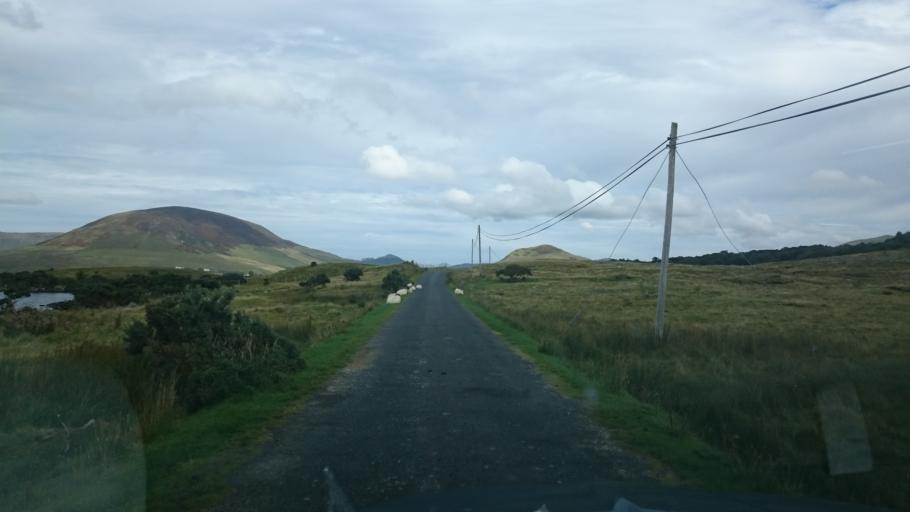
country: IE
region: Connaught
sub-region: Maigh Eo
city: Westport
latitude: 53.9403
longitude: -9.5679
